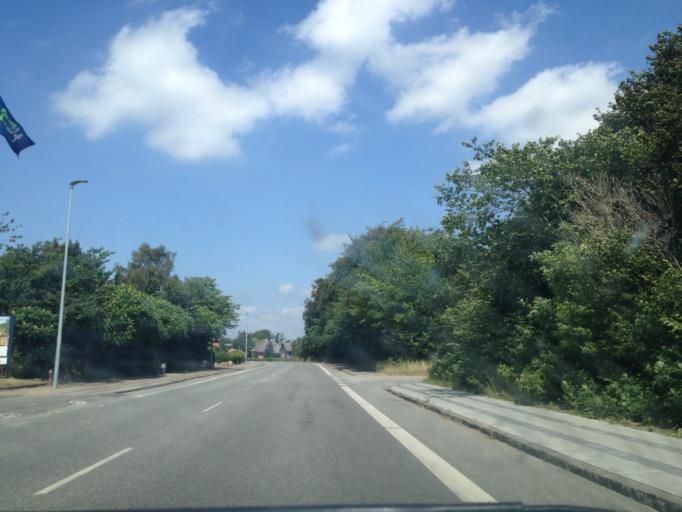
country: DK
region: South Denmark
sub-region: Kolding Kommune
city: Vamdrup
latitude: 55.4292
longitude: 9.2870
